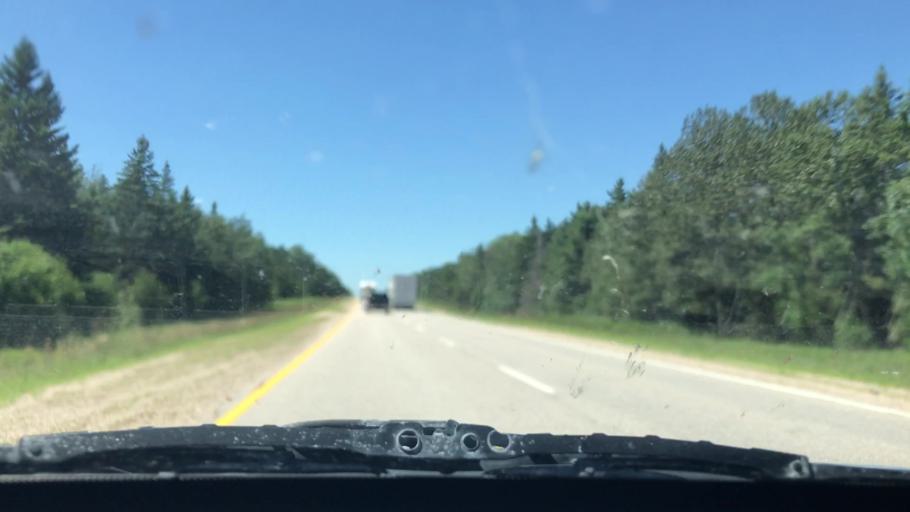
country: CA
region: Manitoba
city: La Broquerie
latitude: 49.6573
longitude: -96.1931
